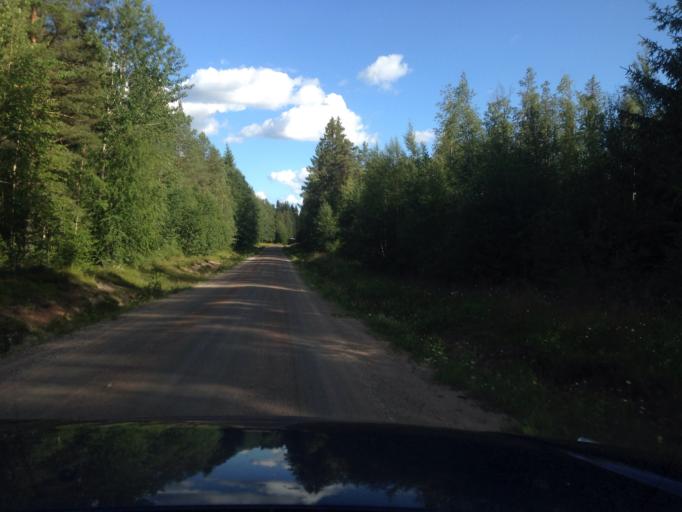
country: SE
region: Dalarna
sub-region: Ludvika Kommun
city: Abborrberget
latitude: 60.2933
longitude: 14.7065
